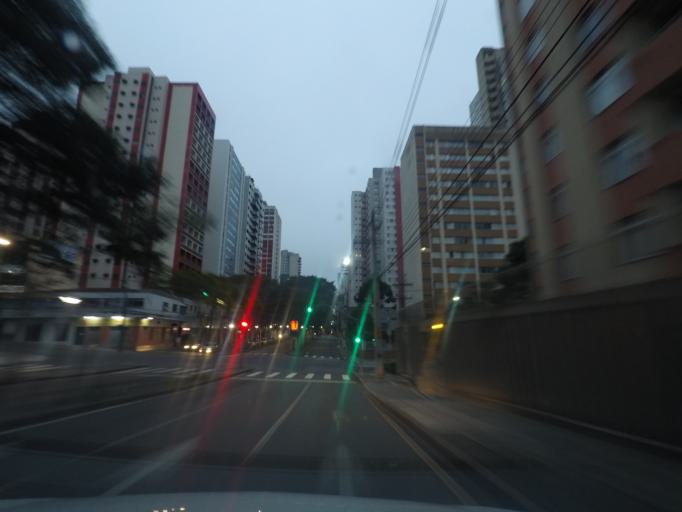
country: BR
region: Parana
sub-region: Curitiba
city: Curitiba
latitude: -25.4313
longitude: -49.2951
